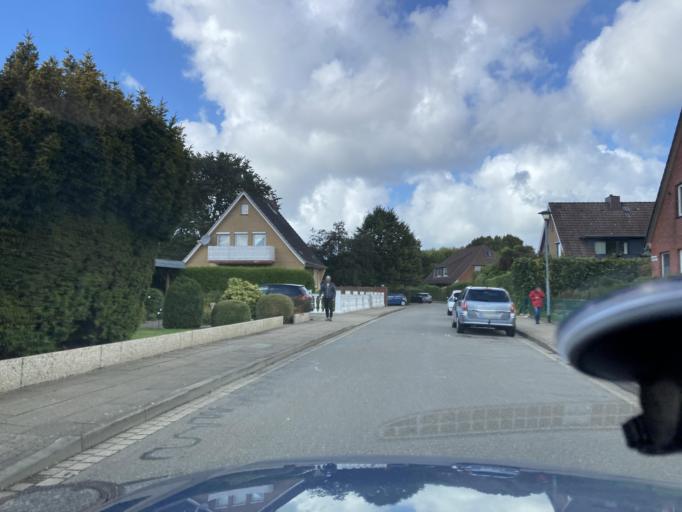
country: DE
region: Schleswig-Holstein
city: Wesseln
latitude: 54.1866
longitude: 9.0844
